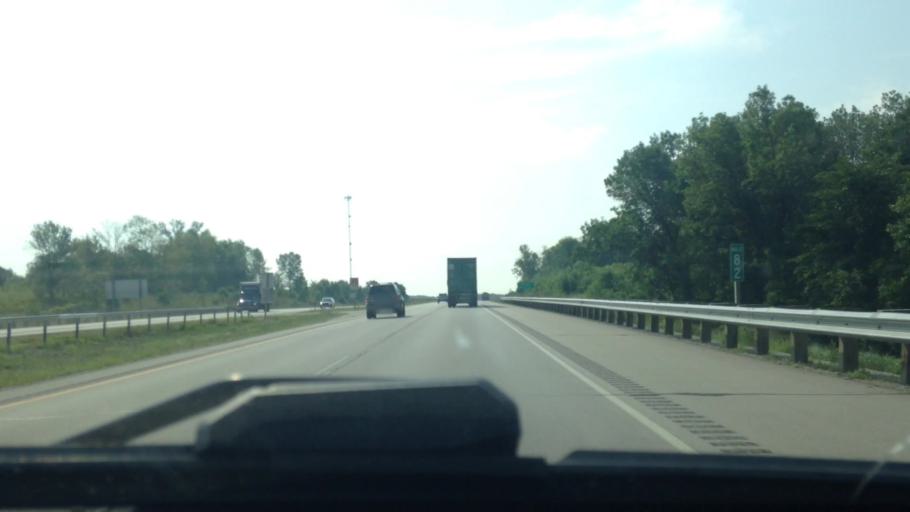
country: US
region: Wisconsin
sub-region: Dodge County
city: Theresa
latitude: 43.5446
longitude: -88.4131
